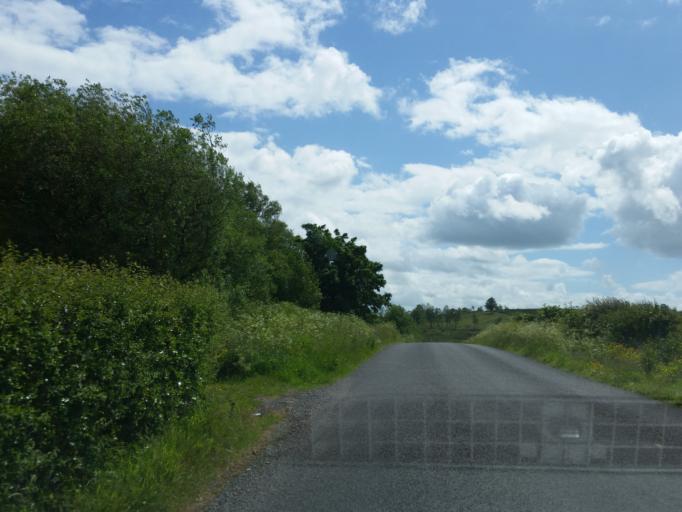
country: GB
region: Northern Ireland
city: Fivemiletown
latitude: 54.3572
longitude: -7.3043
